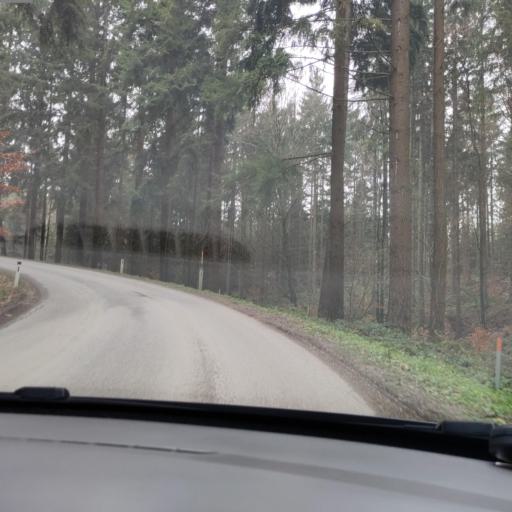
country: AT
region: Lower Austria
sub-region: Politischer Bezirk Sankt Polten
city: Neidling
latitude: 48.2707
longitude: 15.5197
